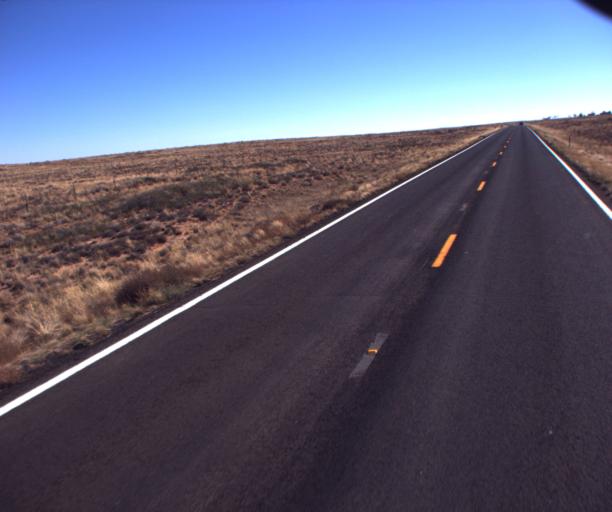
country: US
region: Arizona
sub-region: Coconino County
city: Tuba City
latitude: 35.9664
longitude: -110.9527
